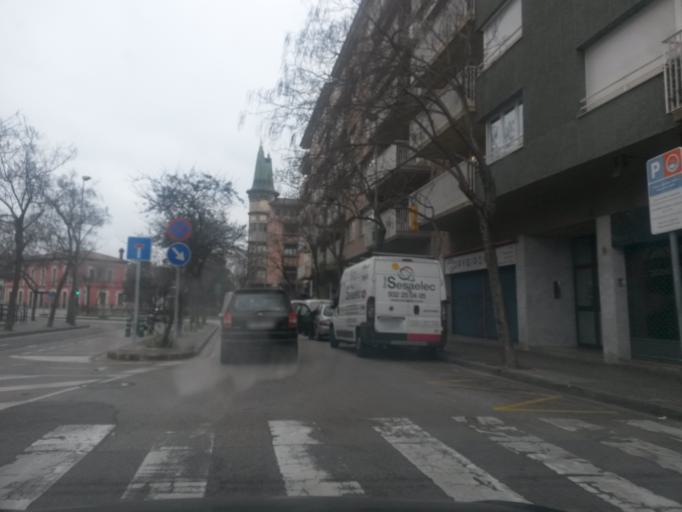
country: ES
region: Catalonia
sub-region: Provincia de Girona
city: Girona
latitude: 41.9814
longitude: 2.8147
